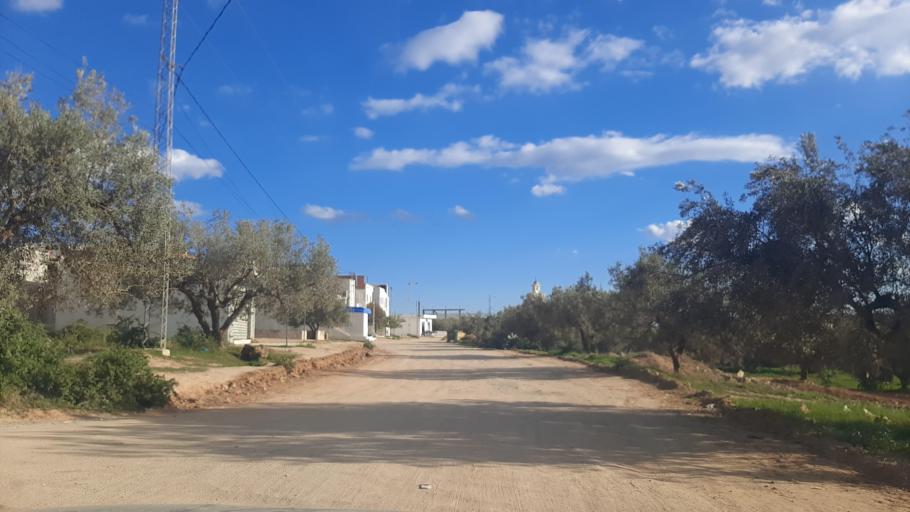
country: TN
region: Nabul
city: Al Hammamat
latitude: 36.4186
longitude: 10.5137
